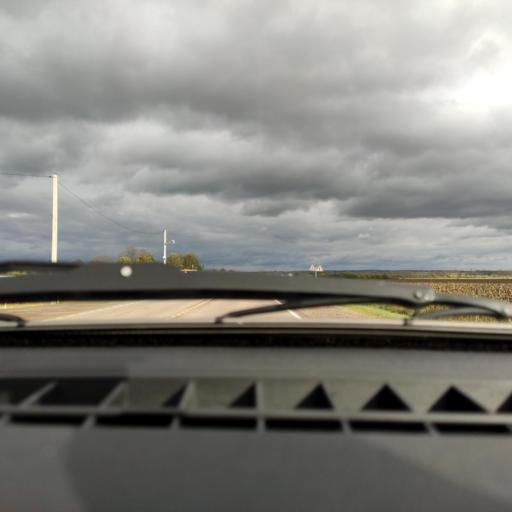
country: RU
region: Bashkortostan
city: Rayevskiy
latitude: 54.0136
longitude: 54.8630
